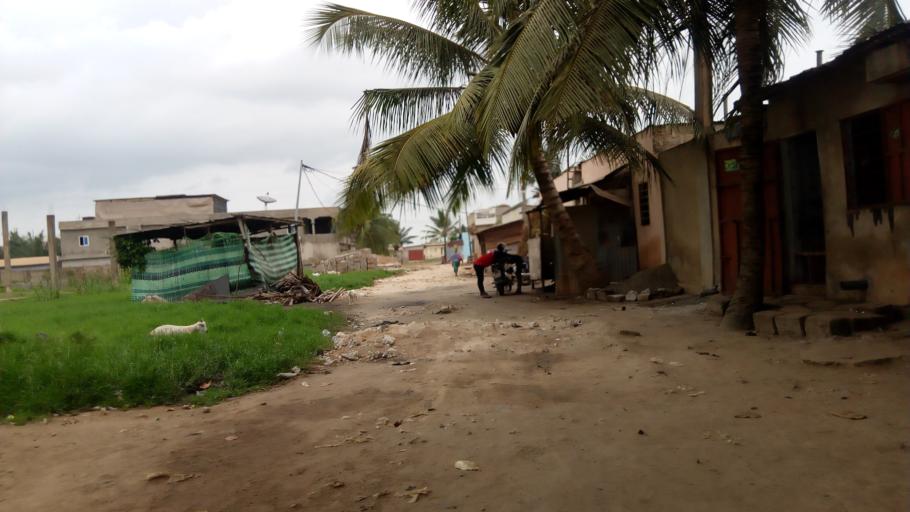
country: TG
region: Maritime
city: Lome
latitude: 6.2530
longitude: 1.2174
